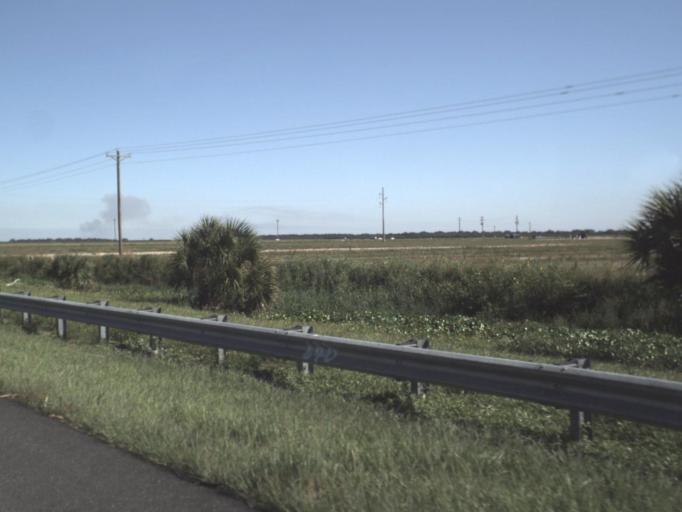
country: US
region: Florida
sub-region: Glades County
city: Moore Haven
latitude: 26.7529
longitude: -81.1166
